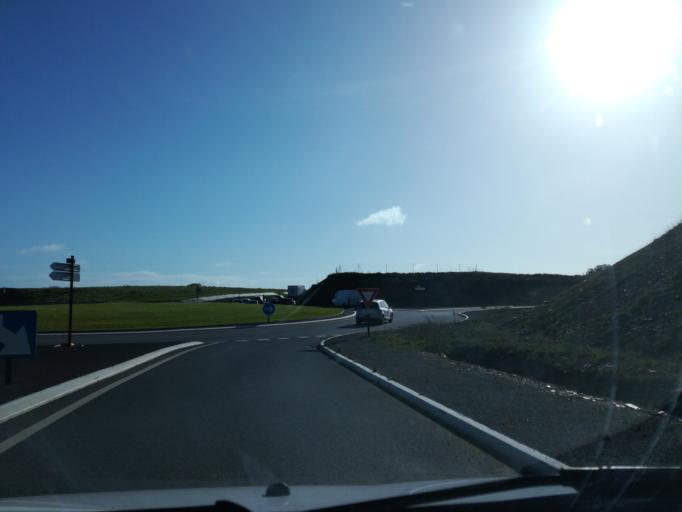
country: FR
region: Brittany
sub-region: Departement d'Ille-et-Vilaine
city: Martigne-Ferchaud
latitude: 47.7994
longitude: -1.2762
